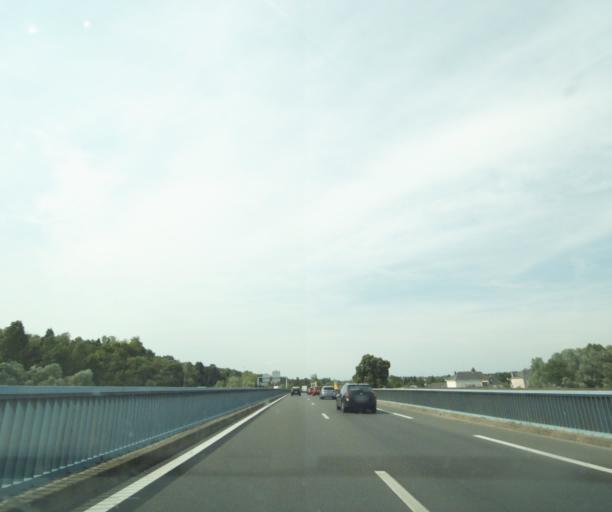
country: FR
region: Centre
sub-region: Departement d'Indre-et-Loire
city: Saint-Cyr-sur-Loire
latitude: 47.3921
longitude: 0.6478
